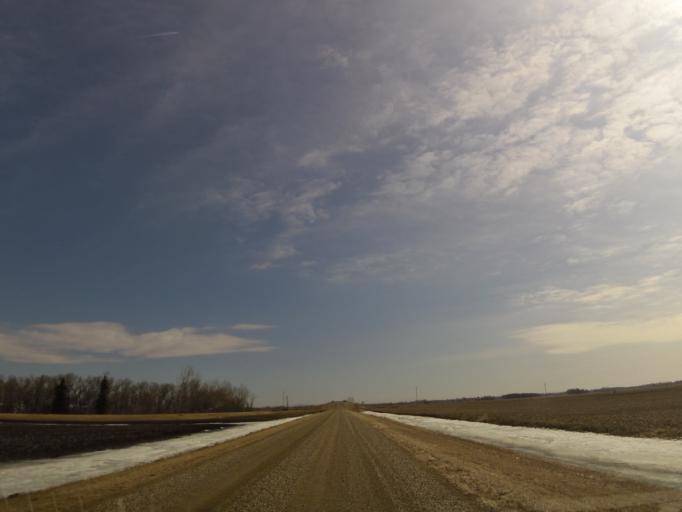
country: US
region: North Dakota
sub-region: Walsh County
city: Grafton
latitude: 48.3243
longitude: -97.1958
